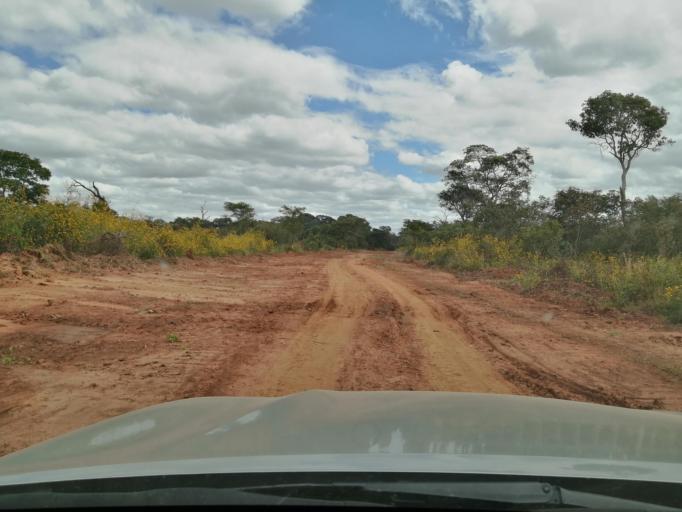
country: ZM
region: Central
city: Mumbwa
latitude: -14.5840
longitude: 27.2141
